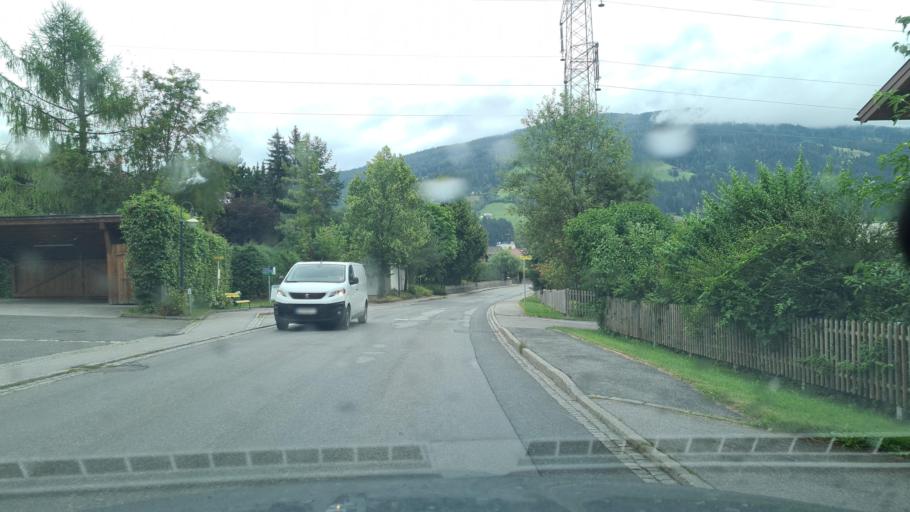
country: AT
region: Salzburg
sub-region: Politischer Bezirk Sankt Johann im Pongau
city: Altenmarkt im Pongau
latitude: 47.3731
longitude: 13.4214
